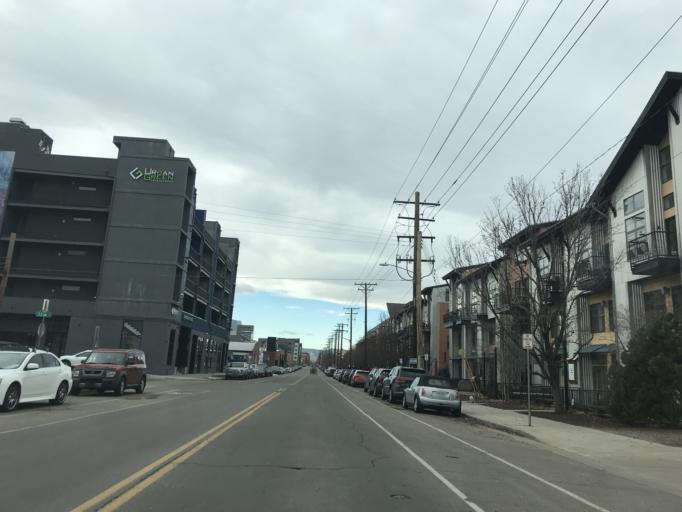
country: US
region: Colorado
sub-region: Denver County
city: Denver
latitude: 39.7658
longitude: -104.9795
